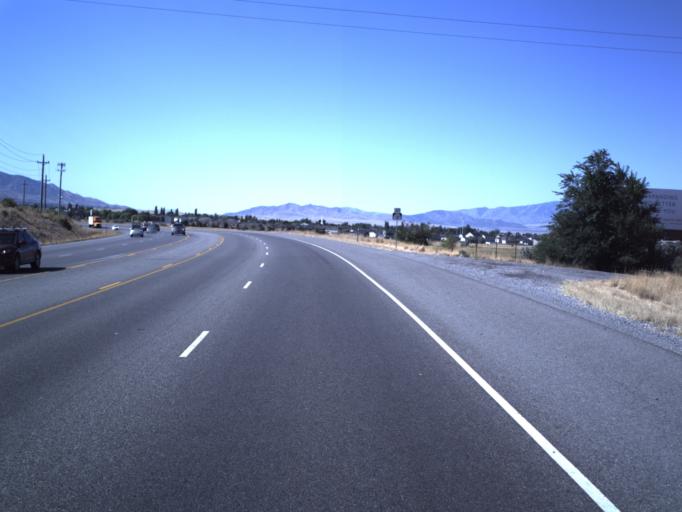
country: US
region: Utah
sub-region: Tooele County
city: Stansbury park
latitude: 40.6615
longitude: -112.2889
